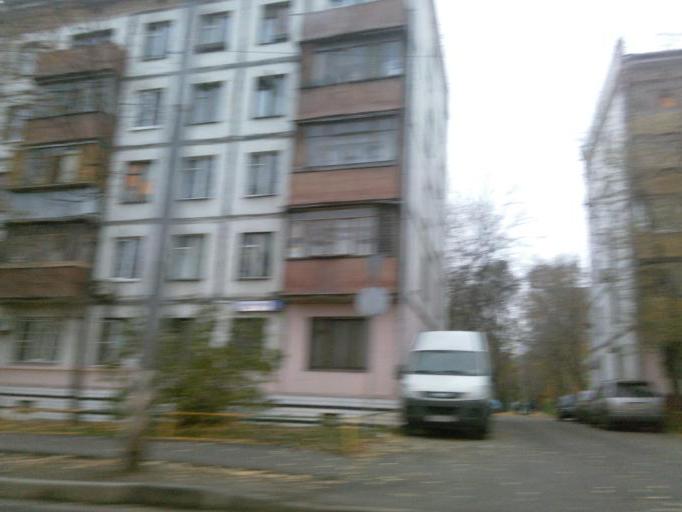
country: RU
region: Moscow
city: Ostankinskiy
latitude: 55.8238
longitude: 37.6023
